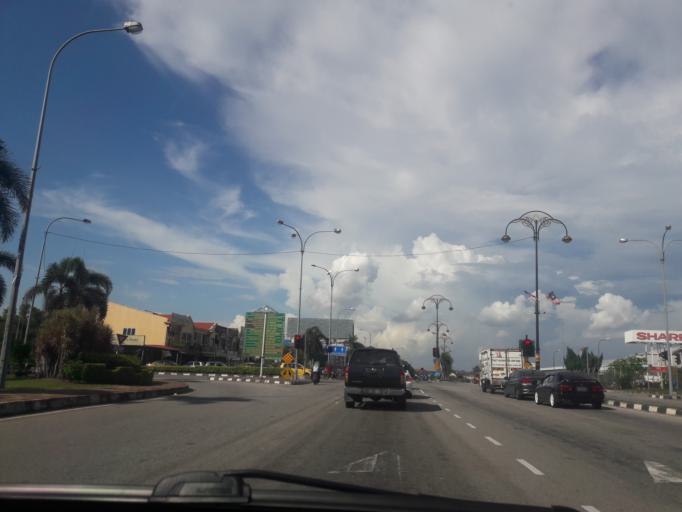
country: MY
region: Kedah
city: Sungai Petani
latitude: 5.6199
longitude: 100.4742
